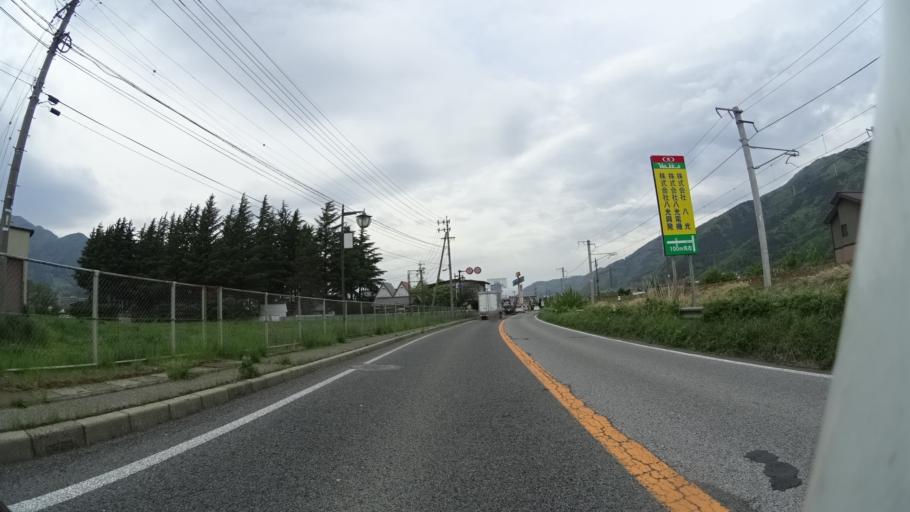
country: JP
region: Nagano
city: Ueda
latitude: 36.4753
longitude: 138.1588
